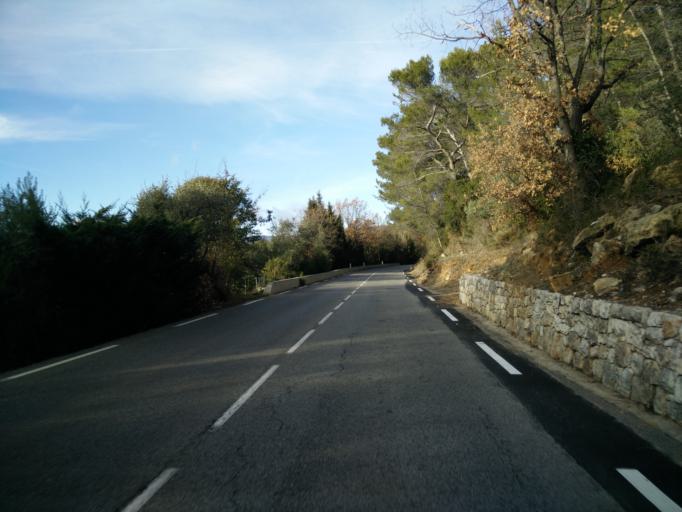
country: FR
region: Provence-Alpes-Cote d'Azur
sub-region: Departement des Alpes-Maritimes
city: Le Tignet
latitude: 43.6364
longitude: 6.8280
